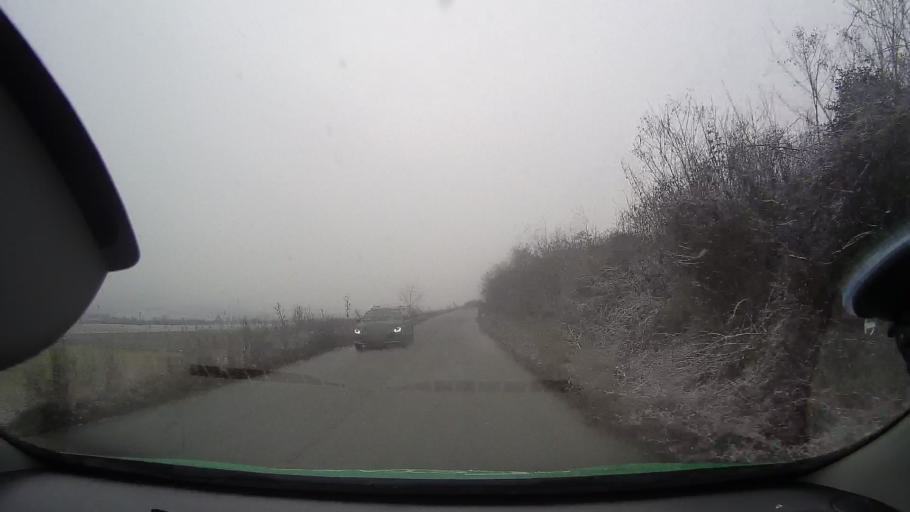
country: RO
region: Alba
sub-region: Comuna Noslac
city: Noslac
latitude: 46.3686
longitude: 23.9285
